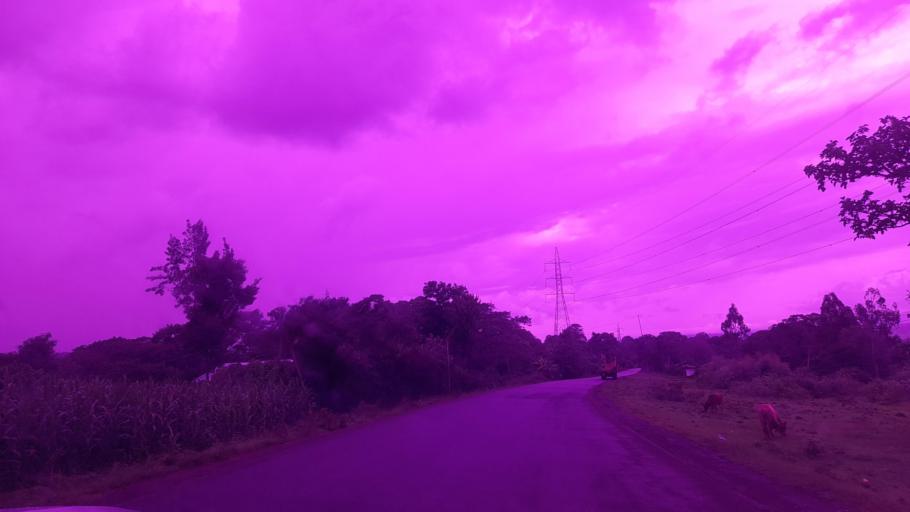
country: ET
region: Oromiya
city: Jima
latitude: 7.7085
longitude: 37.0616
